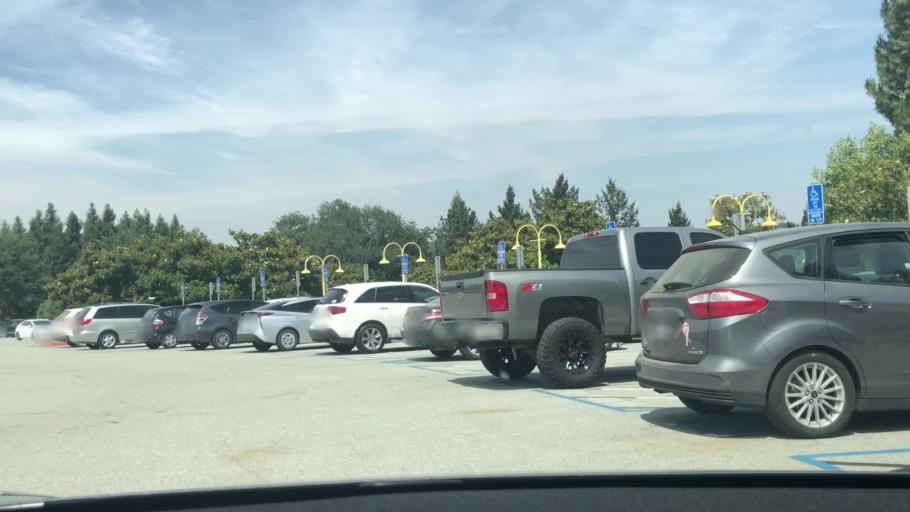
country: US
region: California
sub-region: Santa Clara County
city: Gilroy
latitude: 37.0066
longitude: -121.6295
